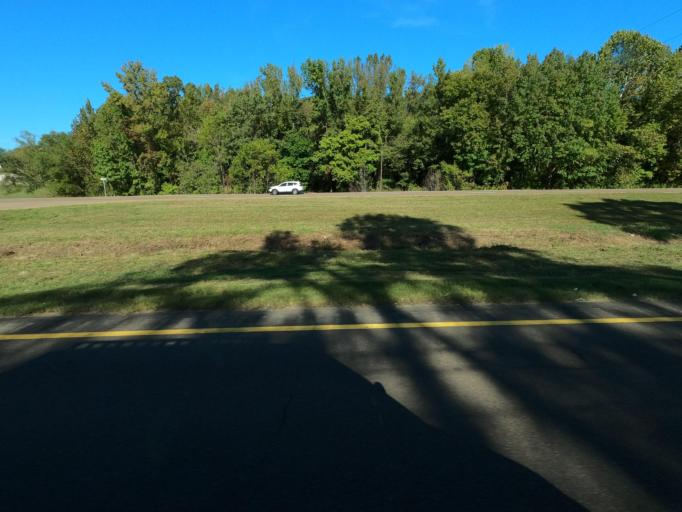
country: US
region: Tennessee
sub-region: Tipton County
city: Atoka
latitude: 35.4615
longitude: -89.7662
